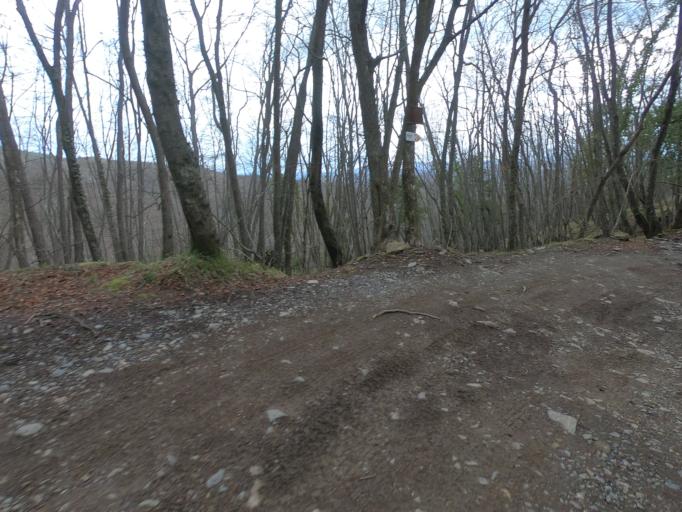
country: IT
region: Liguria
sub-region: Provincia di Imperia
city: Pietrabruna
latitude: 43.9136
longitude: 7.8852
